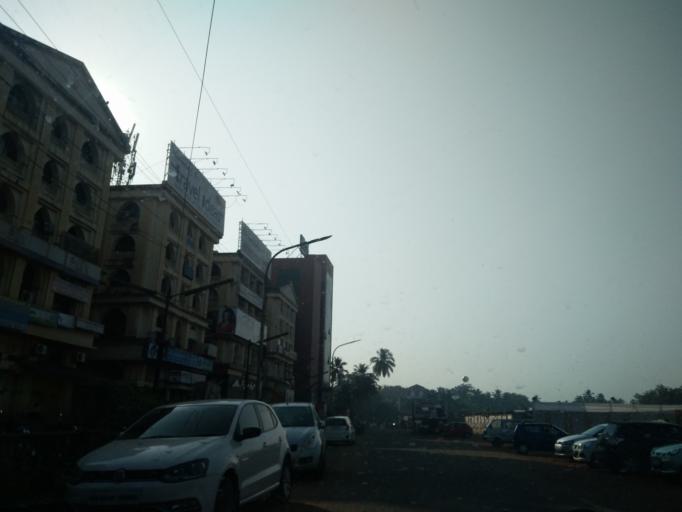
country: IN
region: Goa
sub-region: South Goa
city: Madgaon
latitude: 15.2857
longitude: 73.9569
